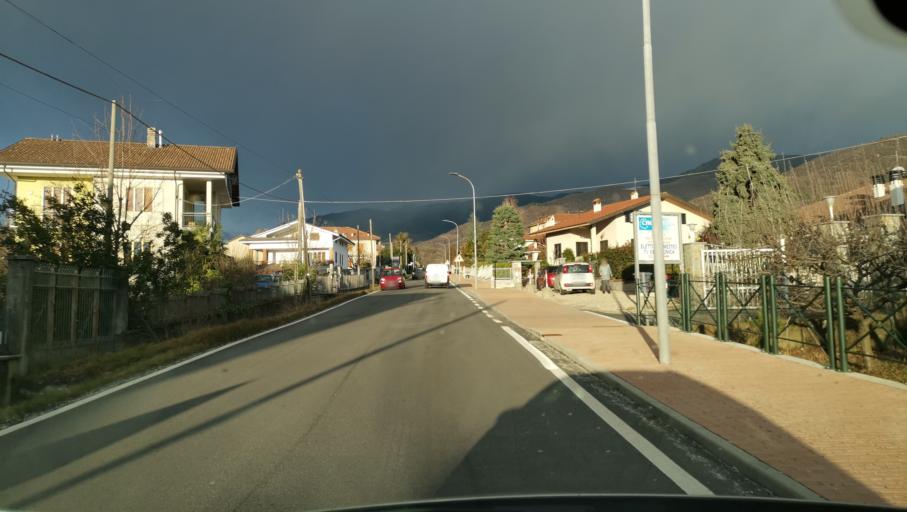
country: IT
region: Piedmont
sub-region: Provincia di Torino
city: Giaveno
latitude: 45.0465
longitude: 7.3450
